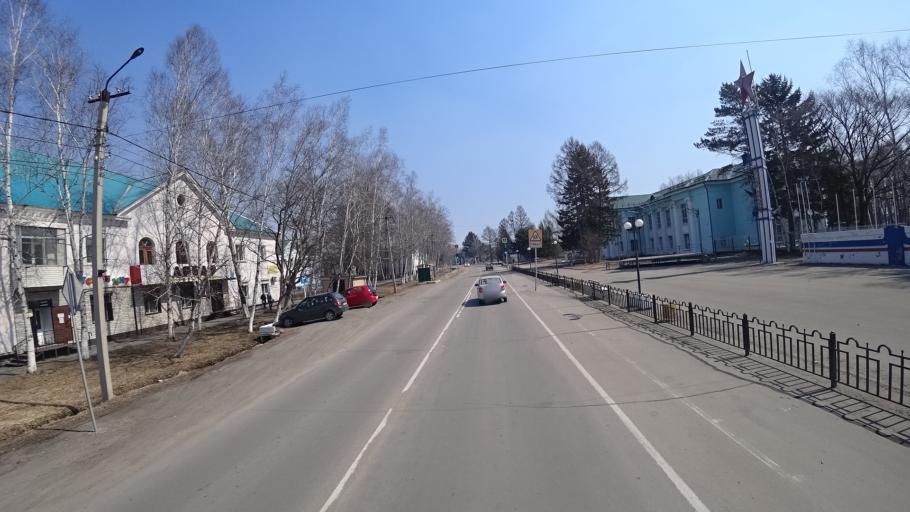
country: RU
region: Amur
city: Novobureyskiy
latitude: 49.7932
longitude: 129.8720
